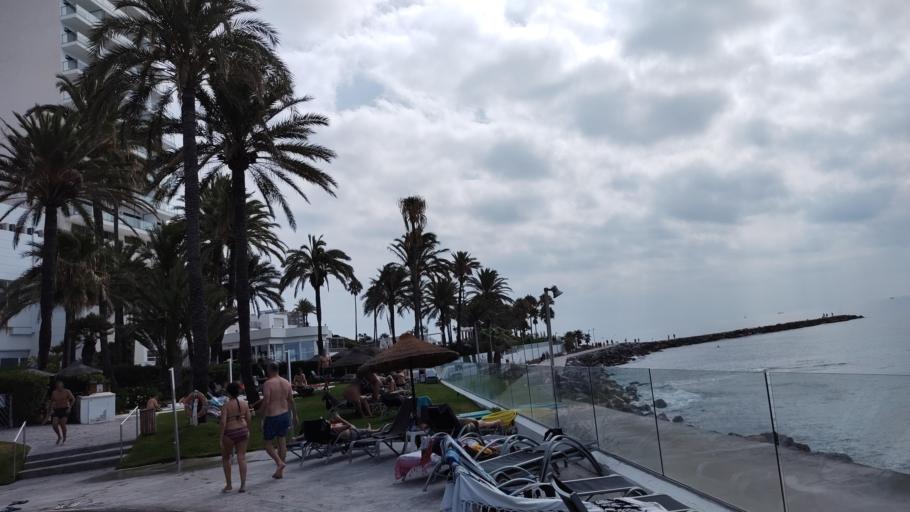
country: ES
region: Andalusia
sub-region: Provincia de Malaga
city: Benalmadena
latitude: 36.5793
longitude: -4.5422
